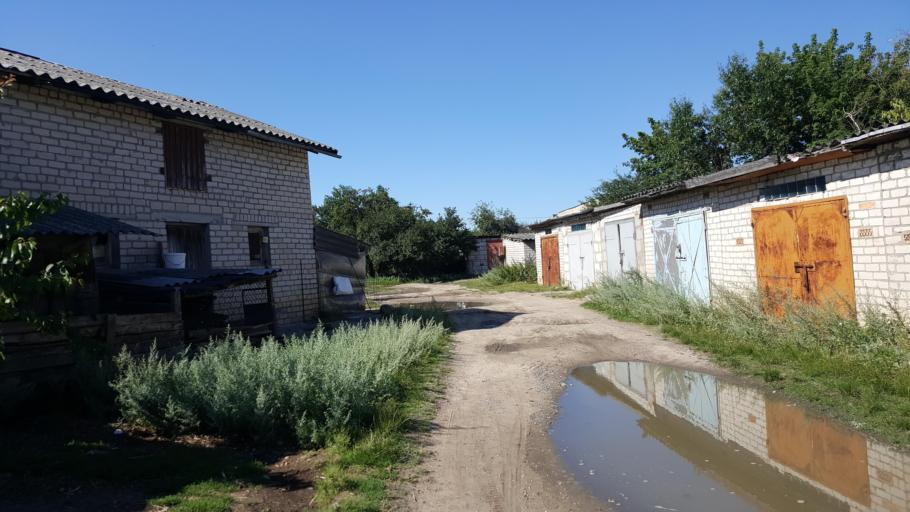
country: BY
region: Brest
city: Charnawchytsy
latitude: 52.2090
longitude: 23.7397
